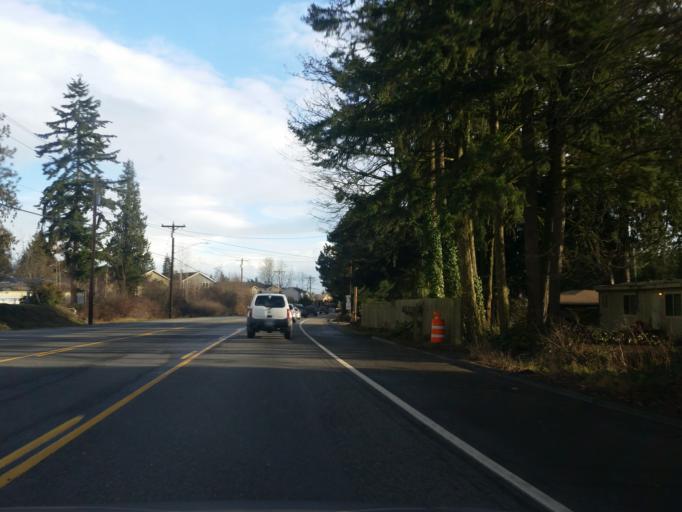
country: US
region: Washington
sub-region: Snohomish County
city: Martha Lake
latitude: 47.8235
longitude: -122.2369
